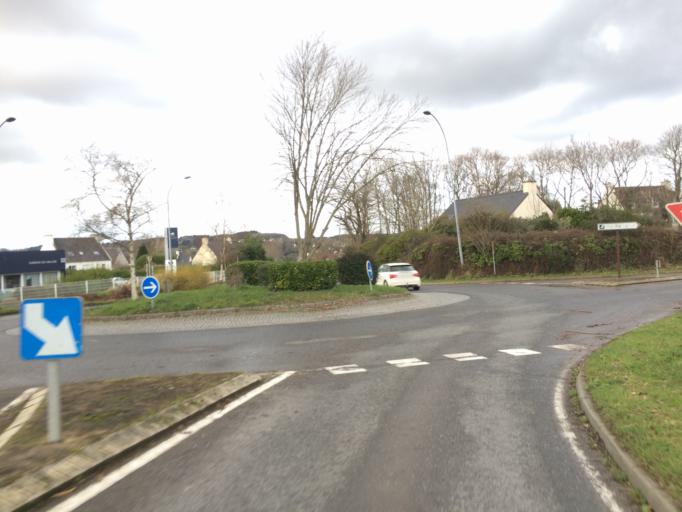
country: FR
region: Brittany
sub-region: Departement du Finistere
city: Daoulas
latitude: 48.3530
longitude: -4.2551
